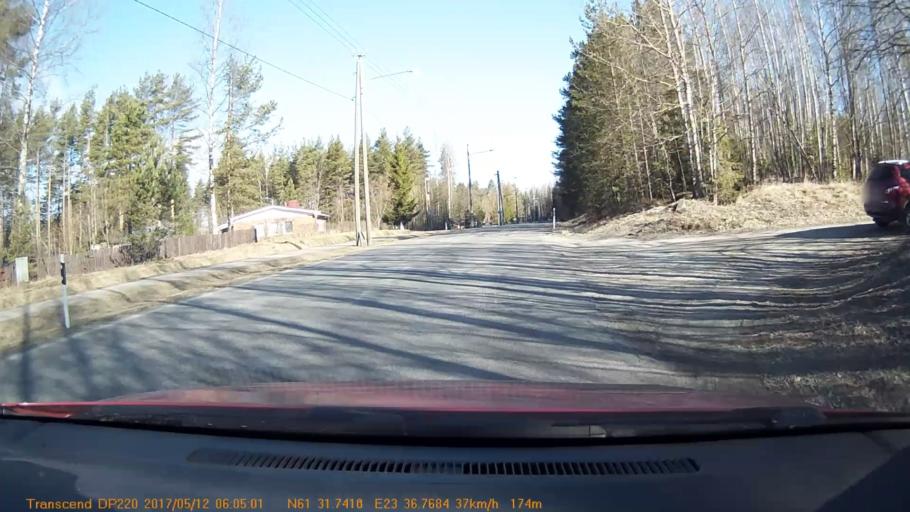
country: FI
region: Pirkanmaa
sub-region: Tampere
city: Yloejaervi
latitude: 61.5289
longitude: 23.6129
